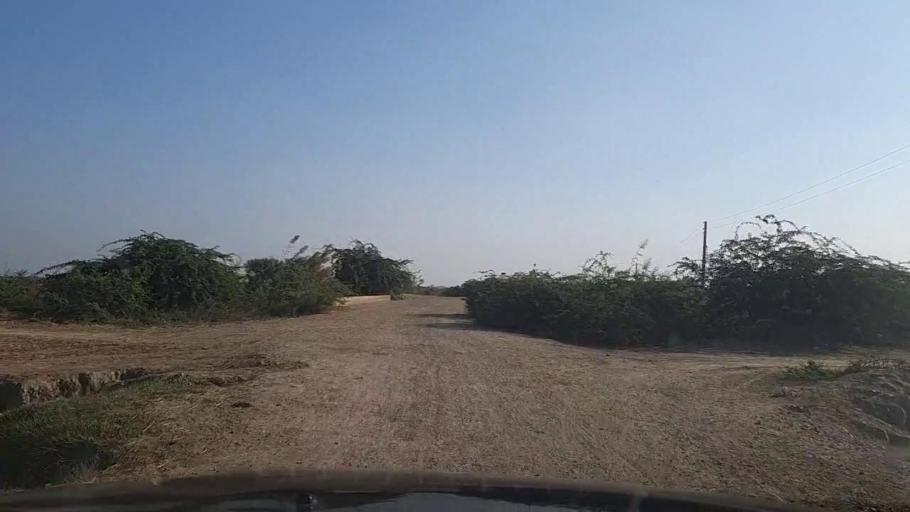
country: PK
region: Sindh
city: Gharo
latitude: 24.7085
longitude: 67.7041
